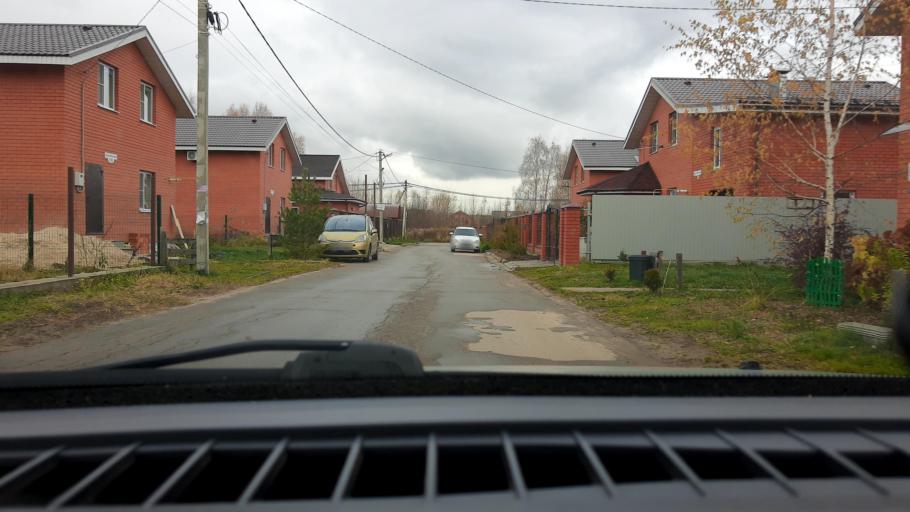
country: RU
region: Nizjnij Novgorod
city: Afonino
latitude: 56.2039
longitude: 44.1248
